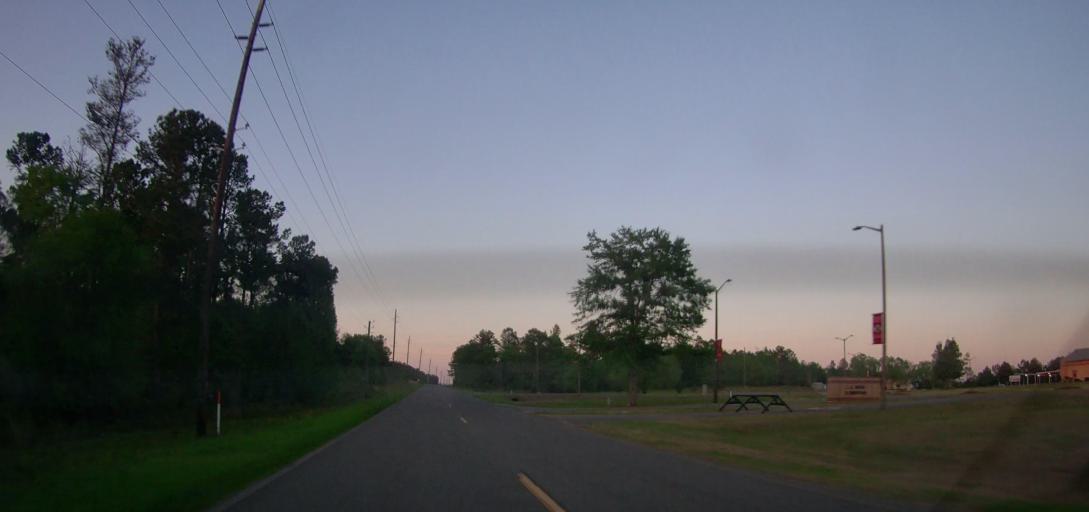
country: US
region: Georgia
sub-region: Marion County
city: Buena Vista
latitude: 32.2879
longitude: -84.5369
